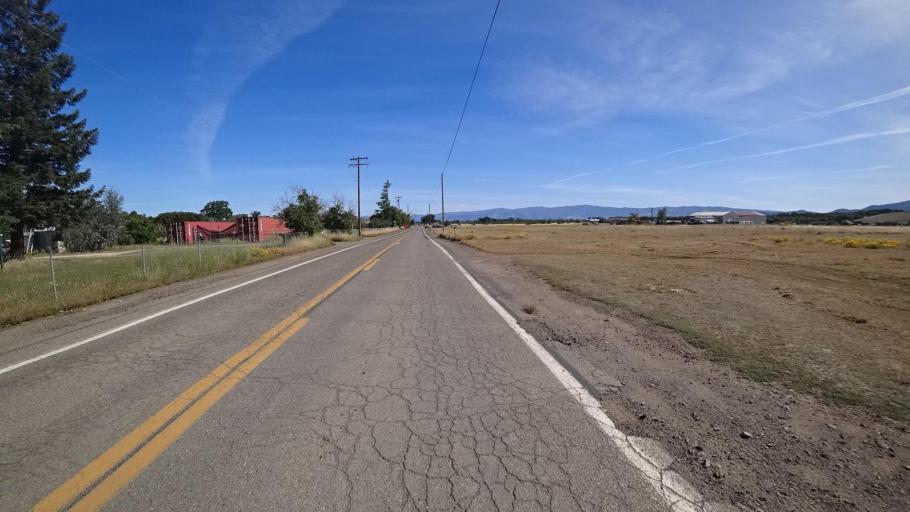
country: US
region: California
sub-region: Lake County
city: Kelseyville
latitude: 38.9575
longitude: -122.8858
